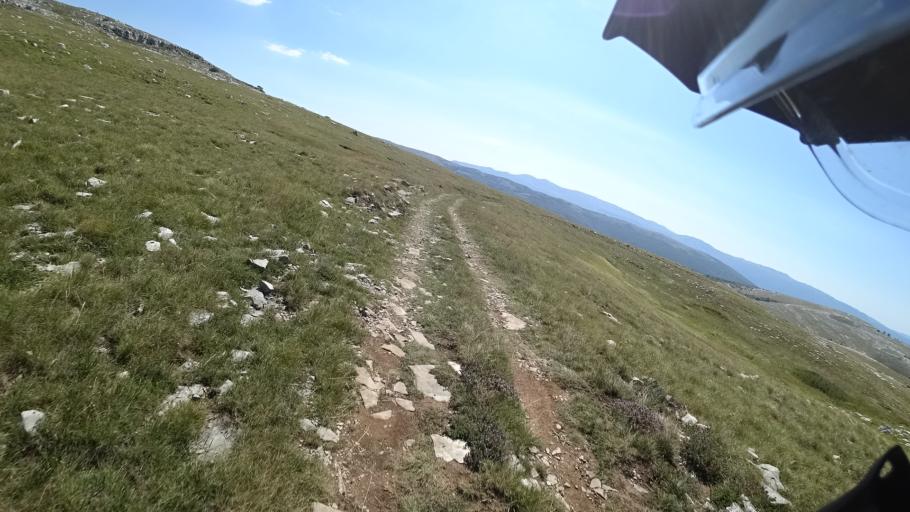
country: HR
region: Splitsko-Dalmatinska
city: Hrvace
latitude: 43.9018
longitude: 16.6059
